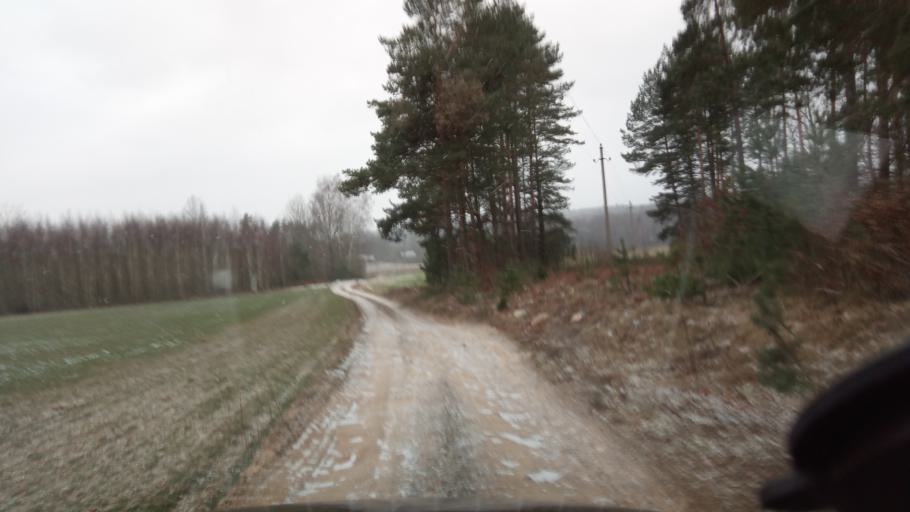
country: LT
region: Alytaus apskritis
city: Varena
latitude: 54.1329
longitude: 24.6884
